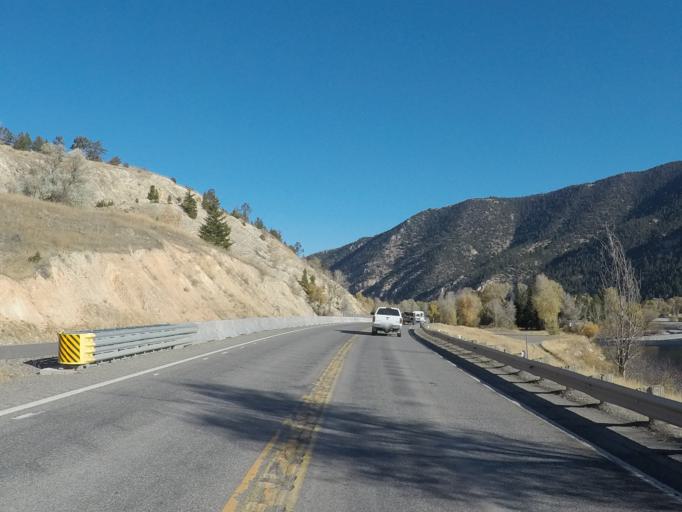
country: US
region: Montana
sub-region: Park County
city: Livingston
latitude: 45.5900
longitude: -110.5724
